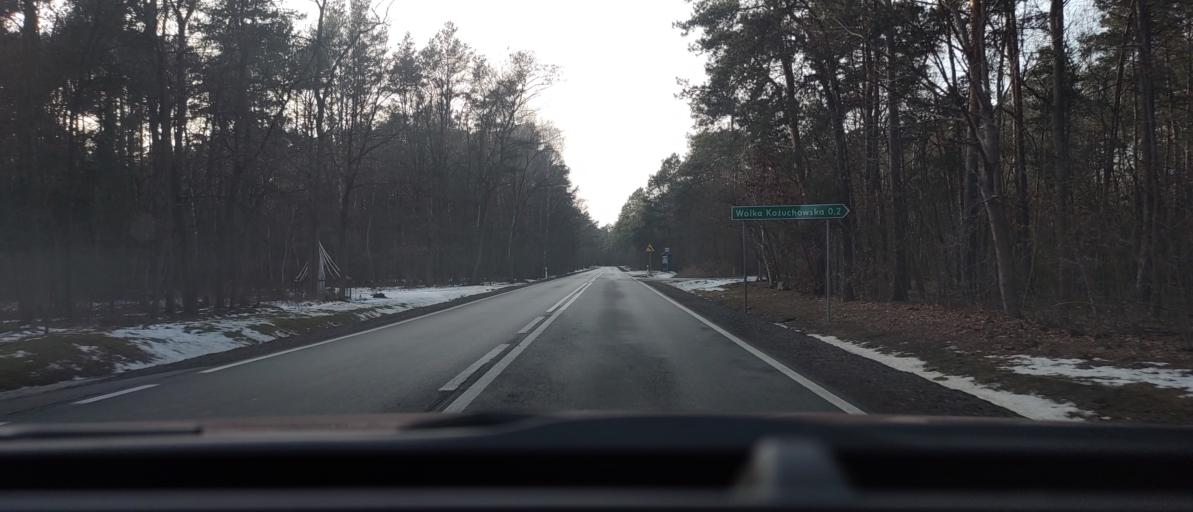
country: PL
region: Masovian Voivodeship
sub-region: Powiat bialobrzeski
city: Wysmierzyce
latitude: 51.6280
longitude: 20.8433
